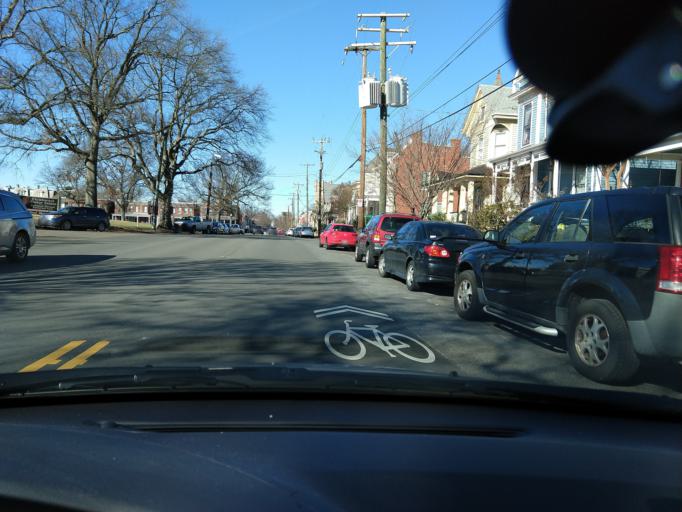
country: US
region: Virginia
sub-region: Henrico County
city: Montrose
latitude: 37.5270
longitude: -77.4112
